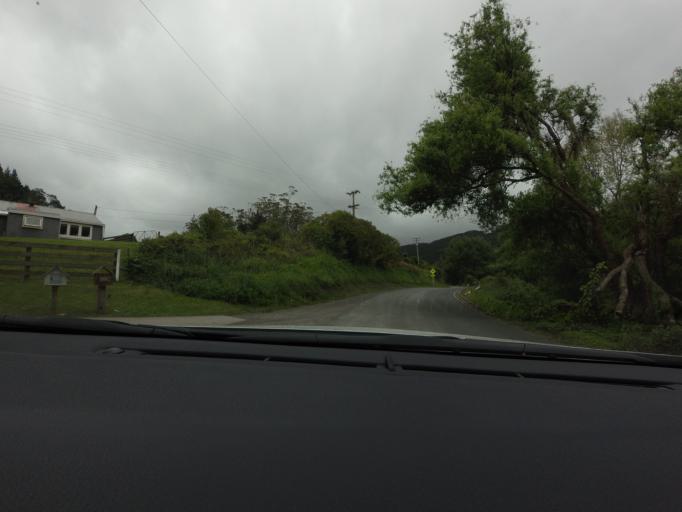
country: NZ
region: Auckland
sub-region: Auckland
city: Warkworth
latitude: -36.4752
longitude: 174.5545
